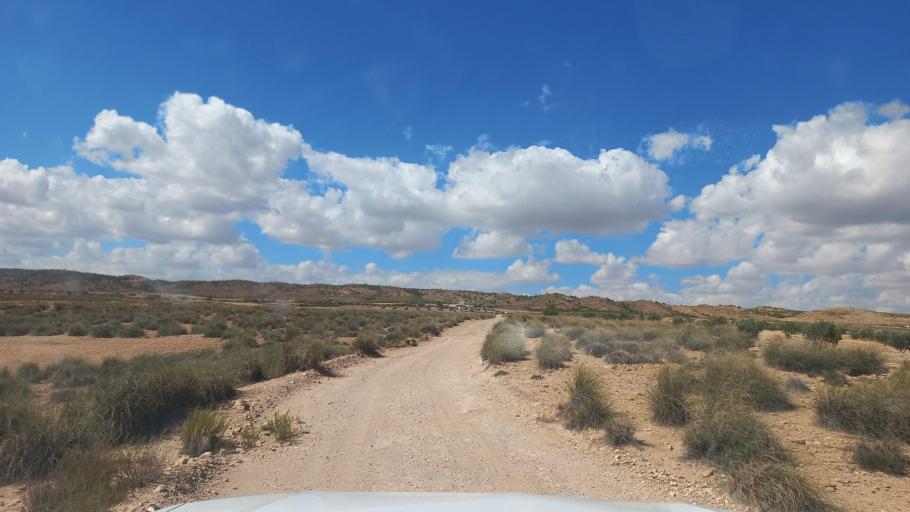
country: TN
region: Al Qasrayn
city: Sbiba
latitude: 35.3594
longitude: 9.0063
